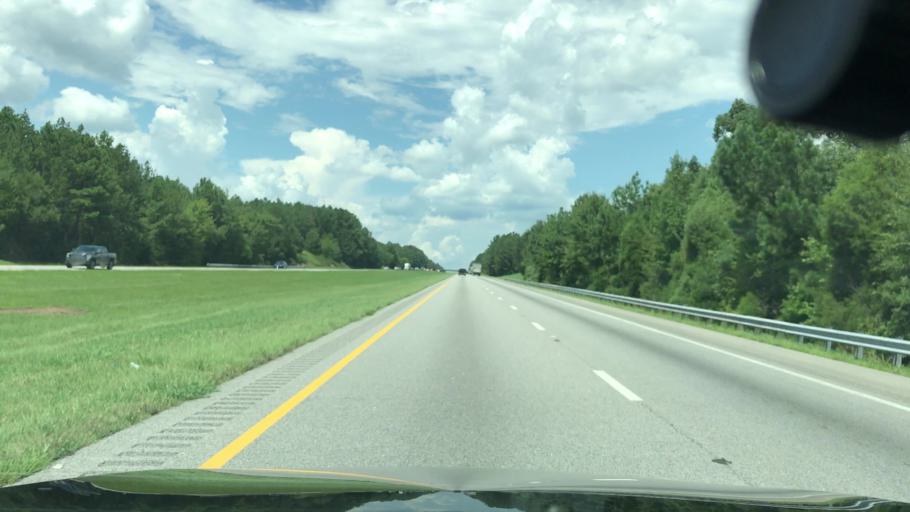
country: US
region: South Carolina
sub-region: Chester County
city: Great Falls
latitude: 34.6654
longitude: -81.0289
